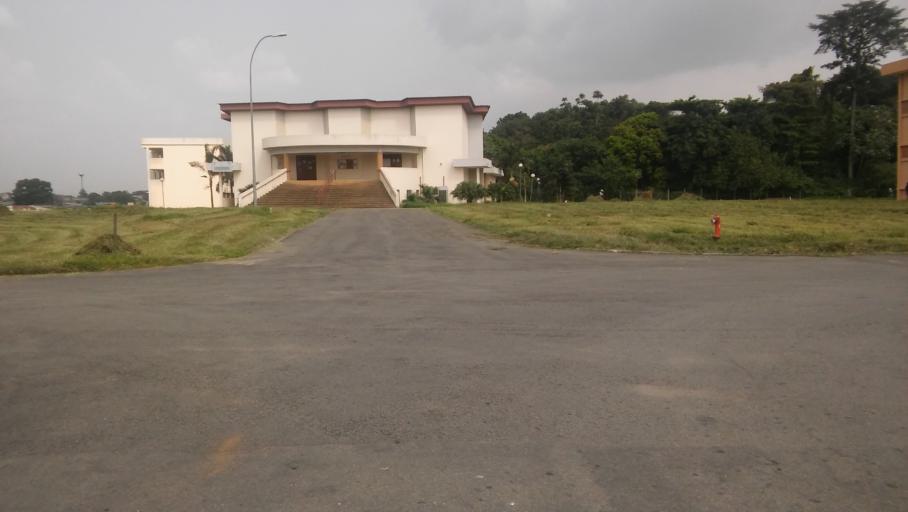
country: CI
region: Lagunes
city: Abidjan
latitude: 5.3479
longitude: -3.9866
